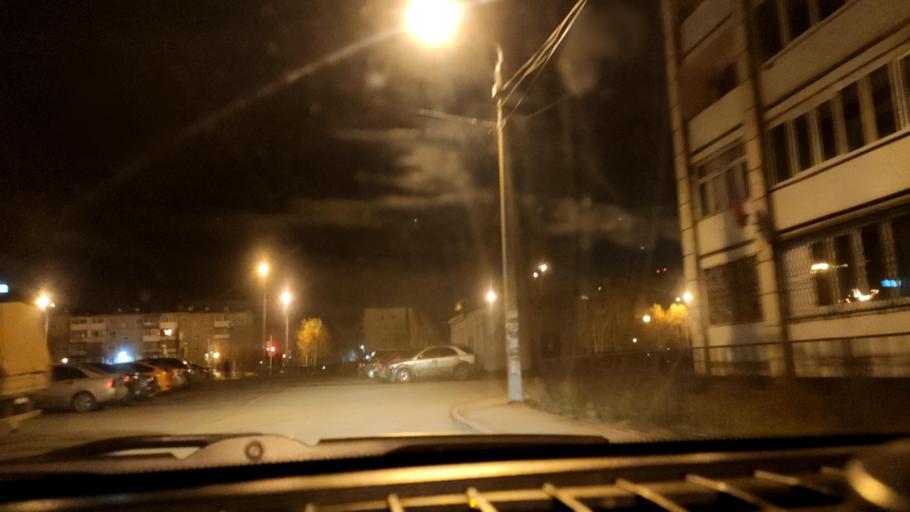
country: RU
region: Perm
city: Perm
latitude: 57.9864
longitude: 56.2234
